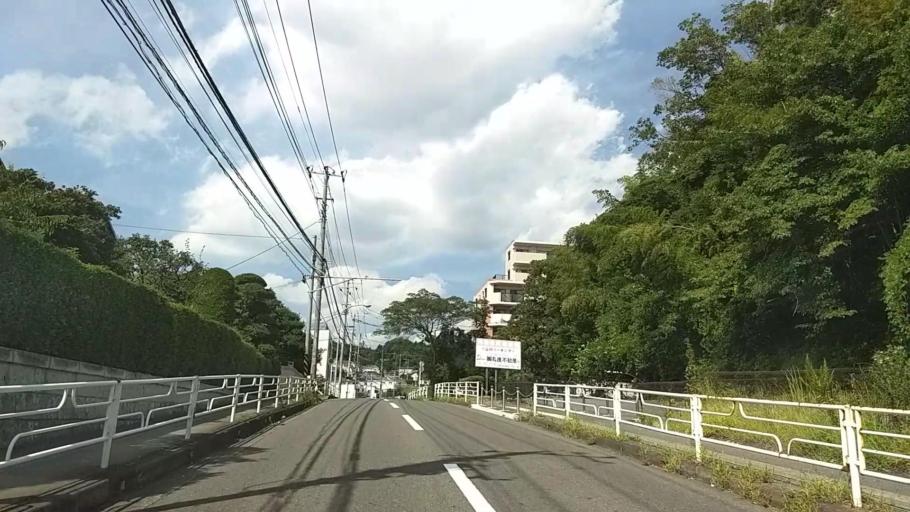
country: JP
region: Kanagawa
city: Yokohama
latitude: 35.5195
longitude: 139.5621
